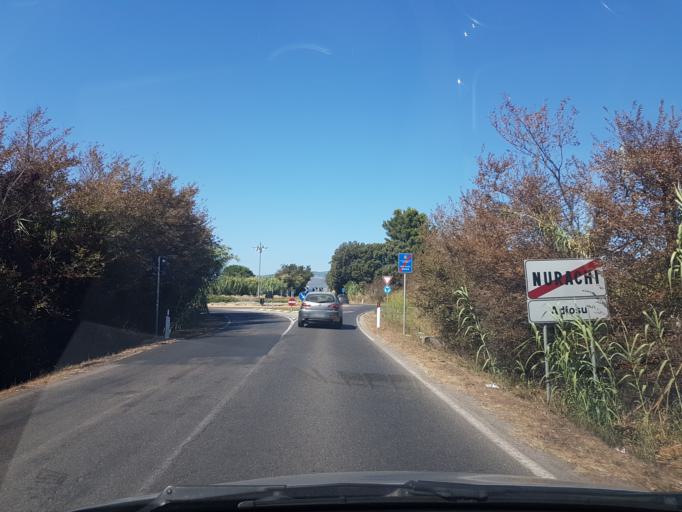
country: IT
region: Sardinia
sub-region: Provincia di Oristano
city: Nurachi
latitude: 39.9816
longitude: 8.5392
